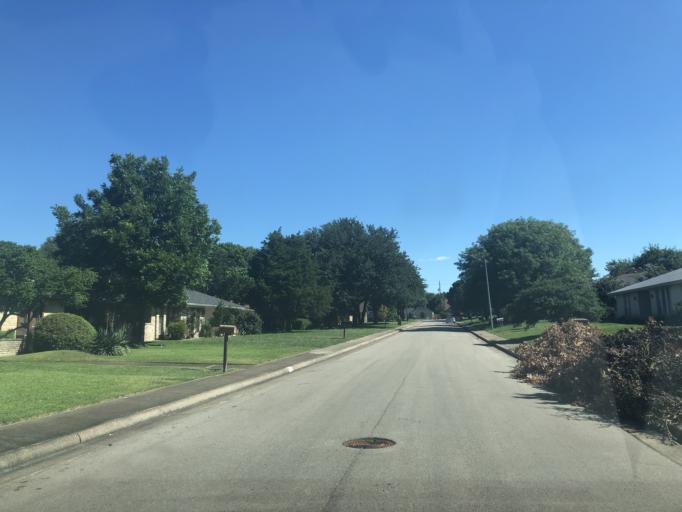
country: US
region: Texas
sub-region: Dallas County
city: Duncanville
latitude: 32.6540
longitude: -96.9318
